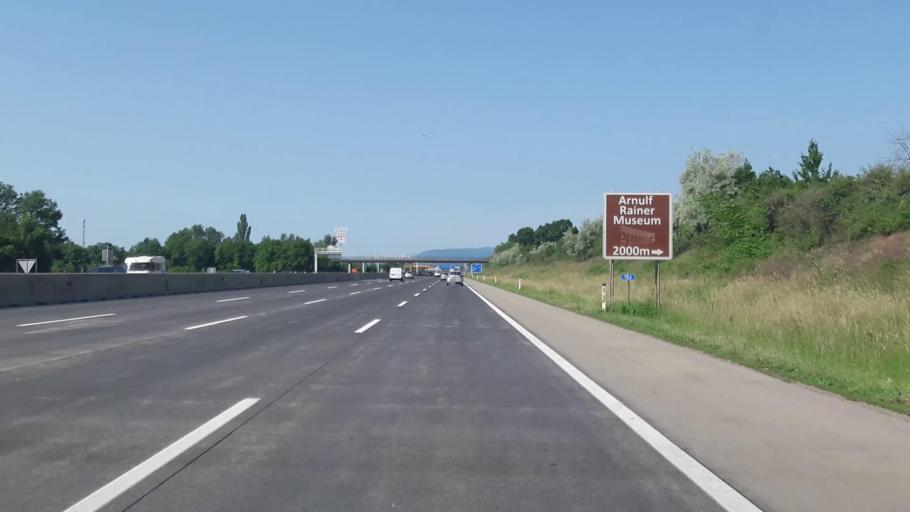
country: AT
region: Lower Austria
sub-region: Politischer Bezirk Baden
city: Traiskirchen
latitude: 48.0006
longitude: 16.2997
